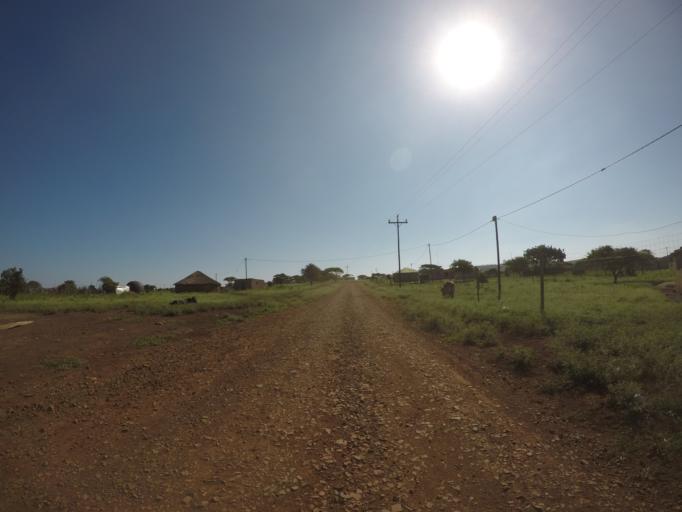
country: ZA
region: KwaZulu-Natal
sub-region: uThungulu District Municipality
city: Empangeni
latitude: -28.5721
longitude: 31.7294
